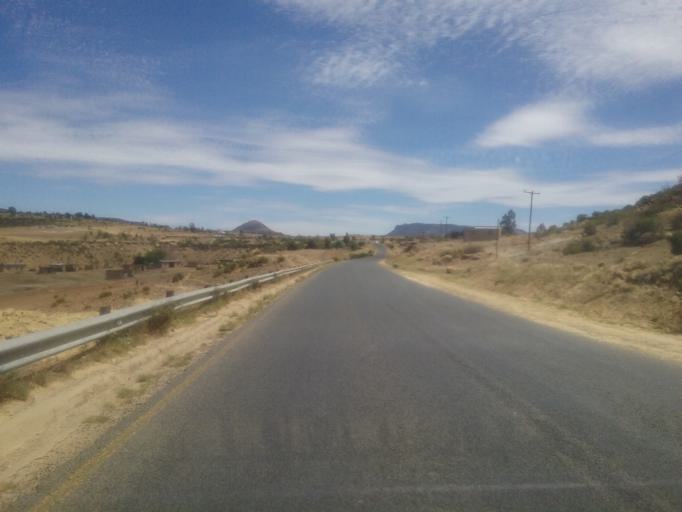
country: LS
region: Mafeteng
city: Mafeteng
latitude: -29.9958
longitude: 27.3379
